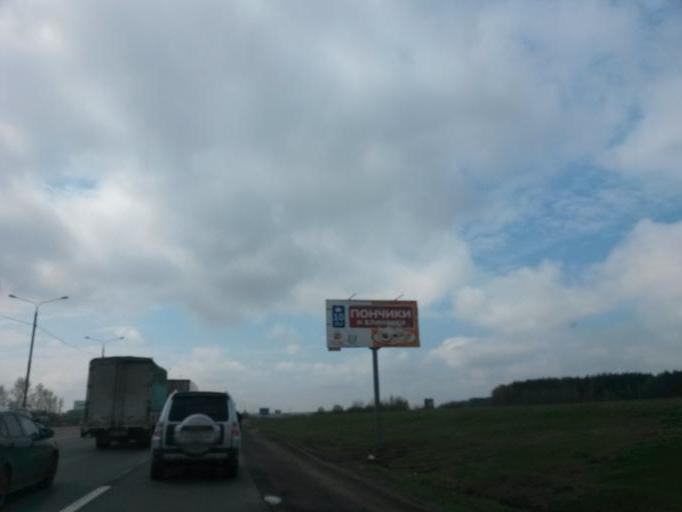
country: RU
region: Moskovskaya
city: Klimovsk
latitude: 55.3428
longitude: 37.5844
